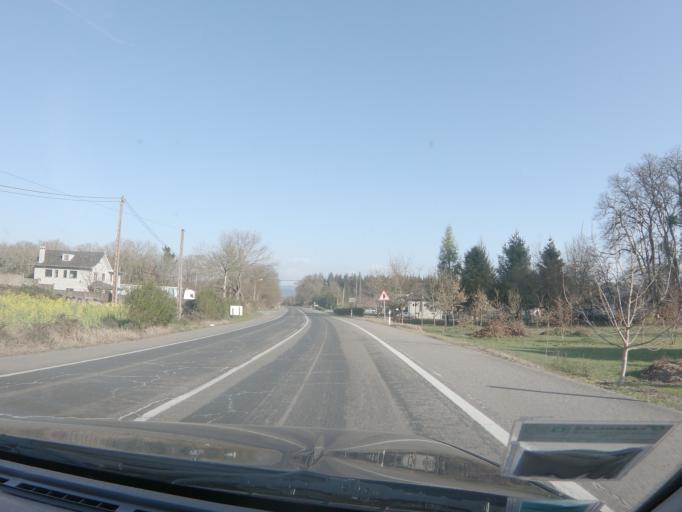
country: ES
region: Galicia
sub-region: Provincia de Lugo
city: Corgo
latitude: 42.9528
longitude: -7.4617
